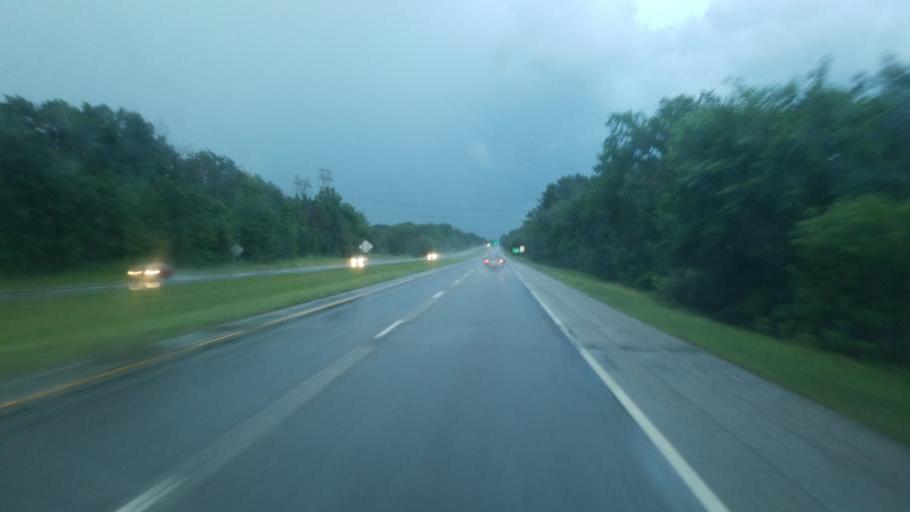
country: US
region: Ohio
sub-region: Wayne County
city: Doylestown
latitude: 40.9701
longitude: -81.6612
